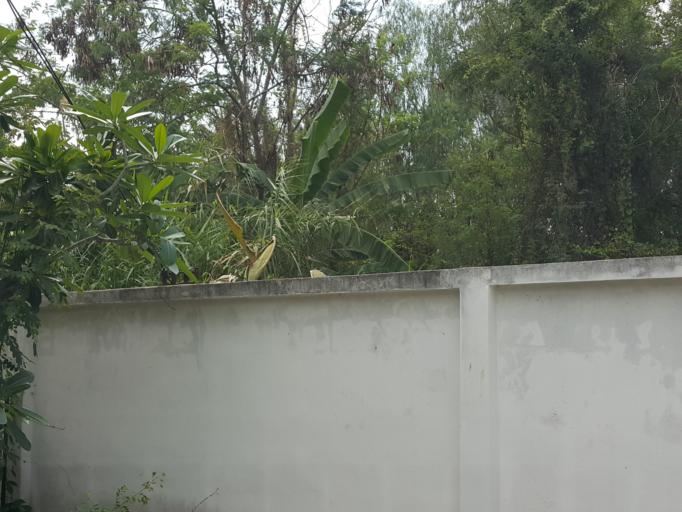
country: TH
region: Chiang Mai
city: Saraphi
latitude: 18.7693
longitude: 99.0508
